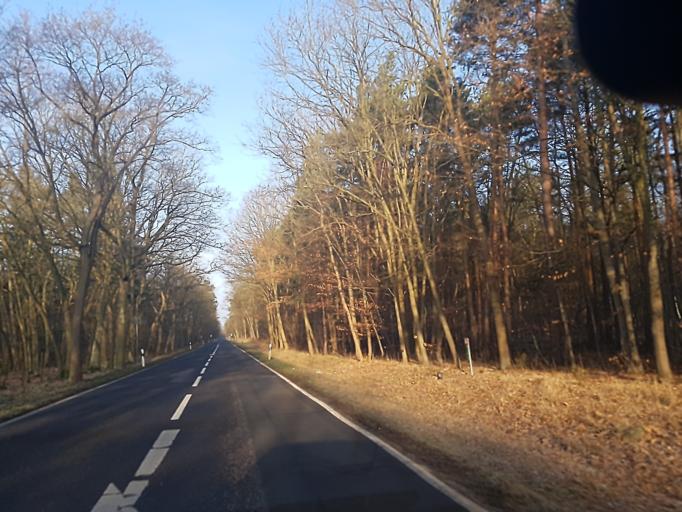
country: DE
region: Brandenburg
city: Bruck
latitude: 52.2157
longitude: 12.7466
